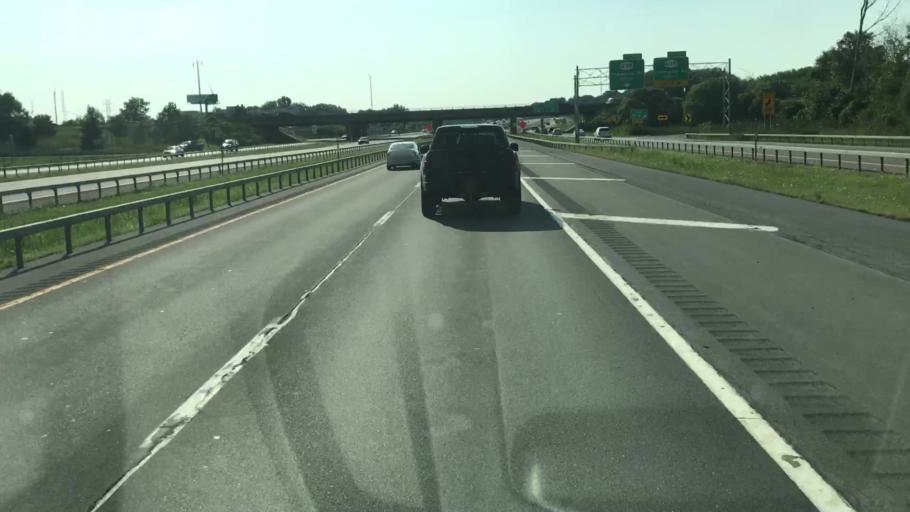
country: US
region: New York
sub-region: Onondaga County
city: East Syracuse
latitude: 43.0566
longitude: -76.0808
